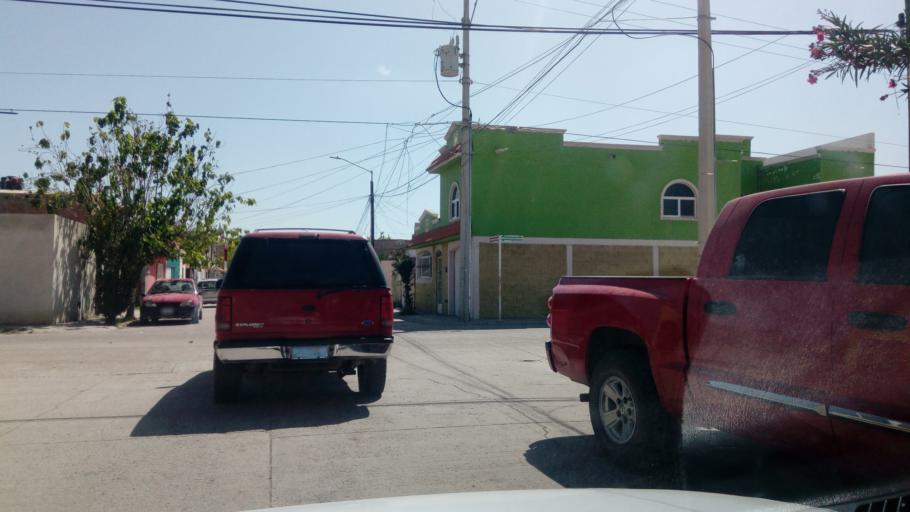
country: MX
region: Durango
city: Victoria de Durango
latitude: 23.9931
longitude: -104.6932
